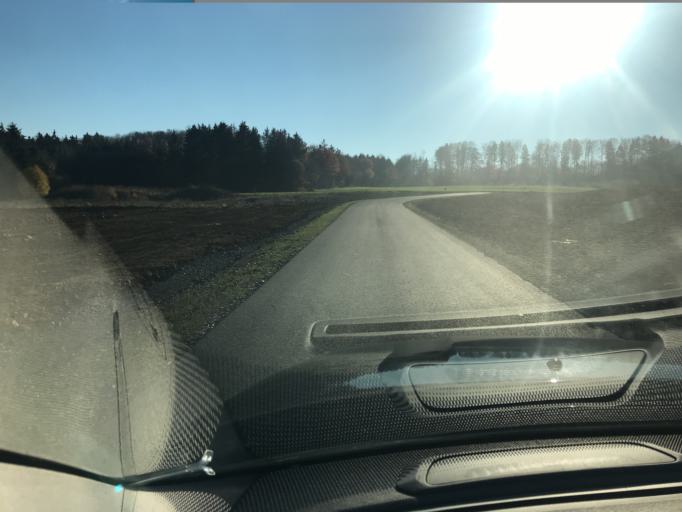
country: DE
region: Rheinland-Pfalz
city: Girod
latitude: 50.4423
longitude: 7.9280
